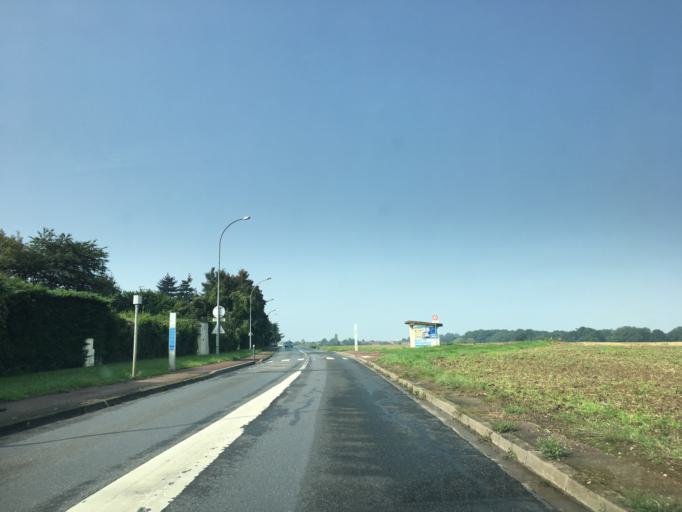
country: FR
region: Ile-de-France
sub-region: Departement du Val-de-Marne
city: Noiseau
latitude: 48.7807
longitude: 2.5612
